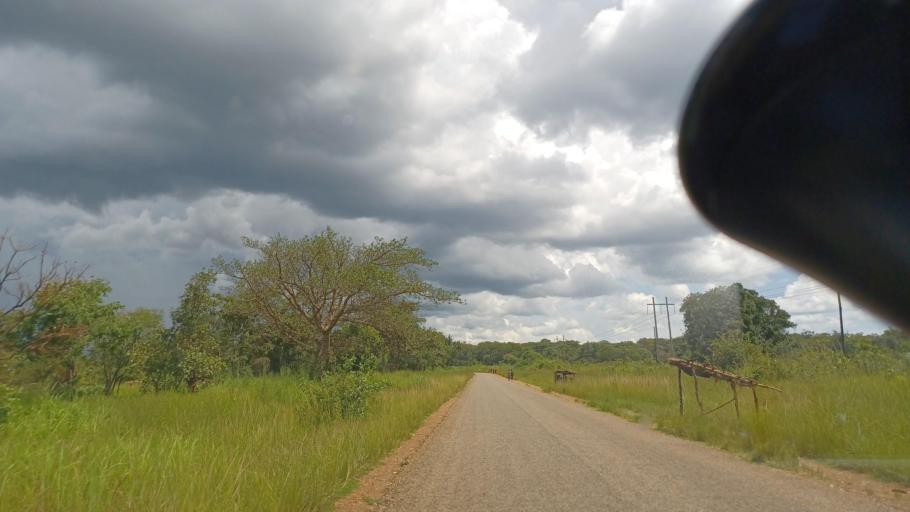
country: ZM
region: North-Western
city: Kasempa
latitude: -12.7769
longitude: 26.0106
